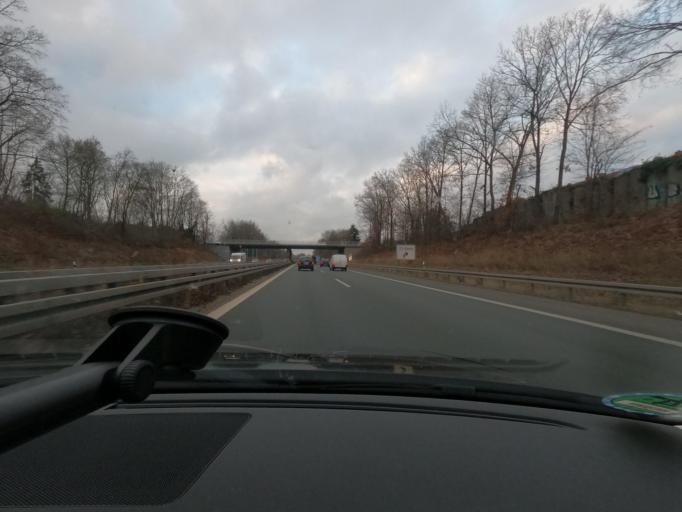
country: DE
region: Bavaria
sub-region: Regierungsbezirk Mittelfranken
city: Furth
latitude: 49.4753
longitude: 11.0122
